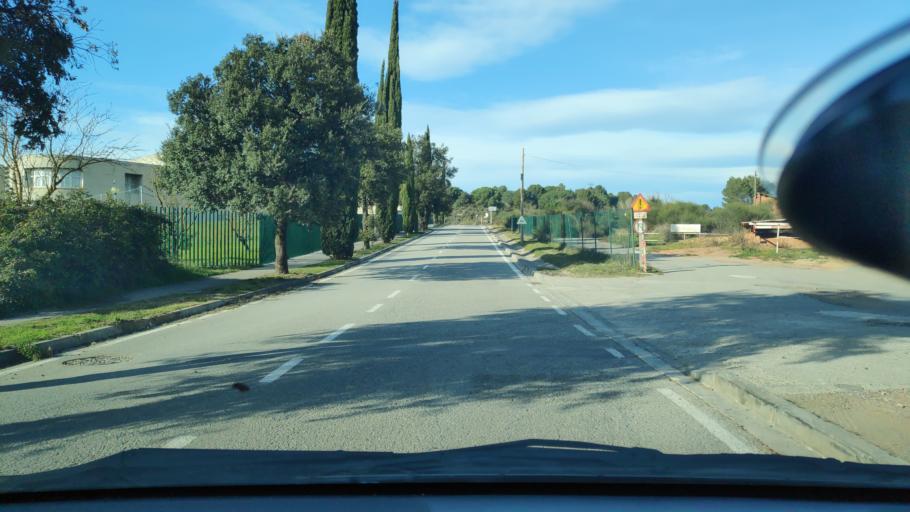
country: ES
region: Catalonia
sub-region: Provincia de Barcelona
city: Rubi
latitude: 41.4962
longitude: 2.0647
